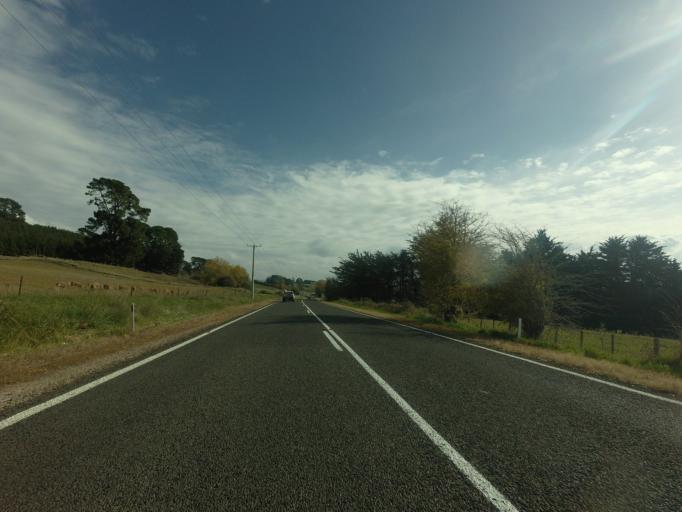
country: AU
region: Tasmania
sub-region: Meander Valley
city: Deloraine
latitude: -41.5256
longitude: 146.6900
